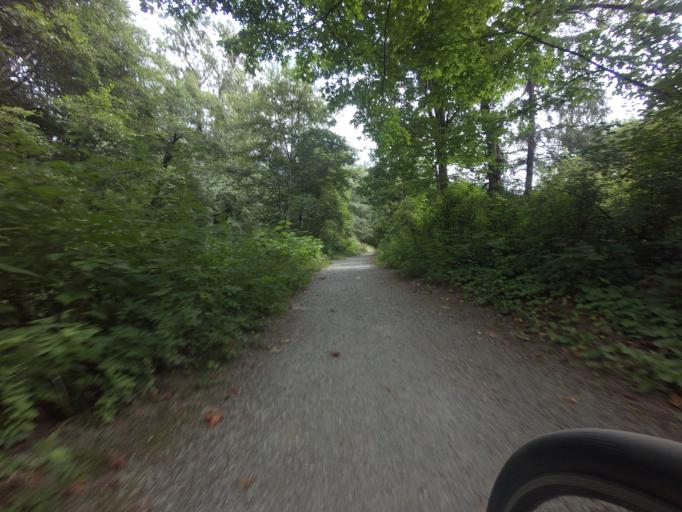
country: CA
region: British Columbia
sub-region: Greater Vancouver Regional District
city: Lions Bay
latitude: 49.7090
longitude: -123.1511
